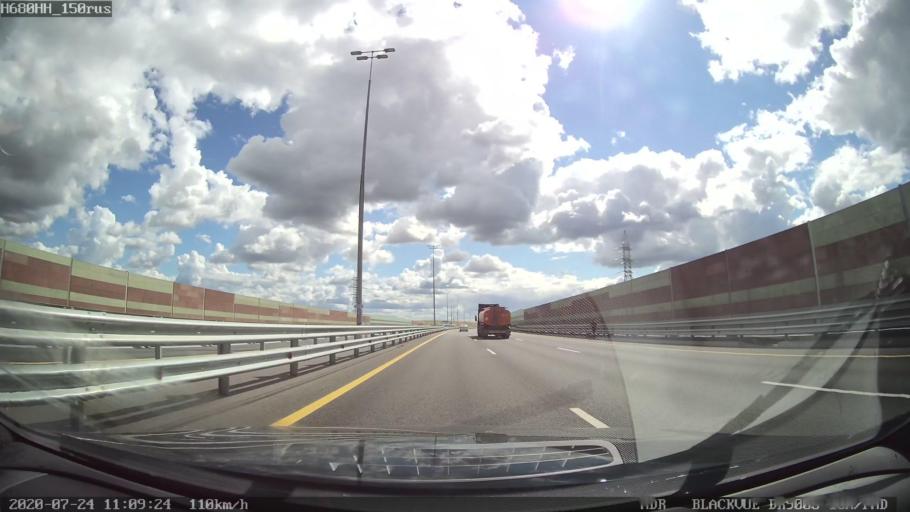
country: RU
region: St.-Petersburg
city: Tyarlevo
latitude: 59.7493
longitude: 30.4743
